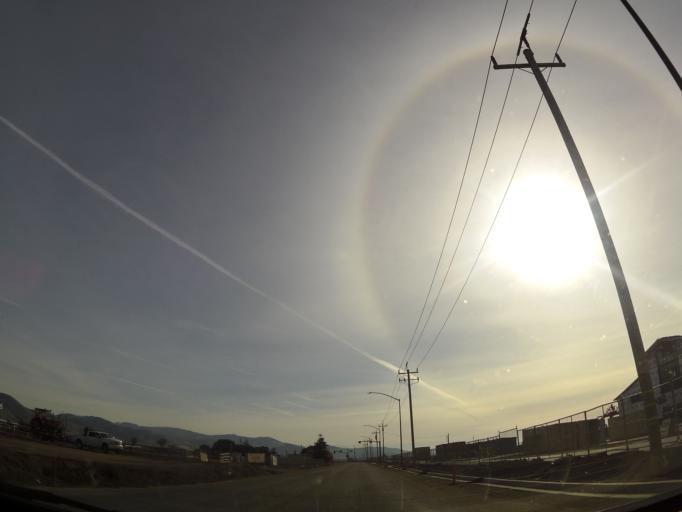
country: US
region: California
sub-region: Monterey County
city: Boronda
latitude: 36.7308
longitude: -121.6299
